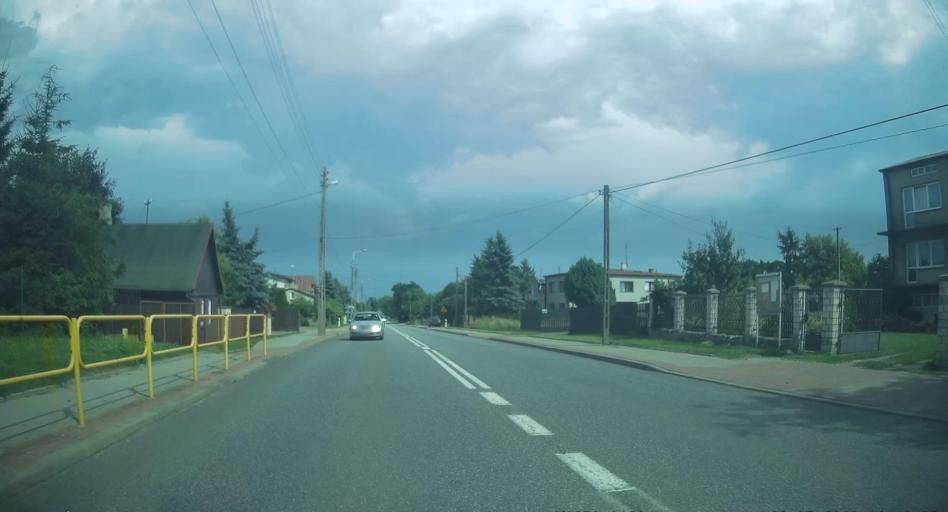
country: PL
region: Lodz Voivodeship
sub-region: Powiat brzezinski
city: Jezow
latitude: 51.8128
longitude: 19.9739
